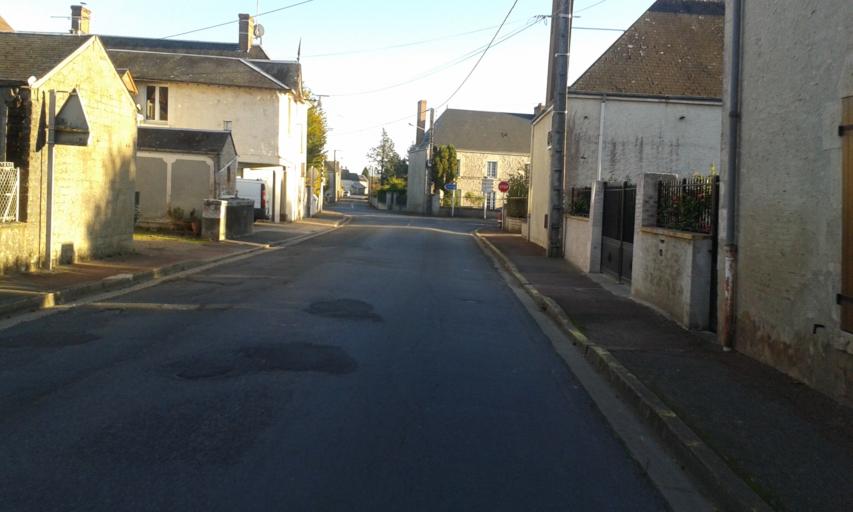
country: FR
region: Centre
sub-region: Departement du Loir-et-Cher
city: Mer
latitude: 47.7952
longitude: 1.5255
